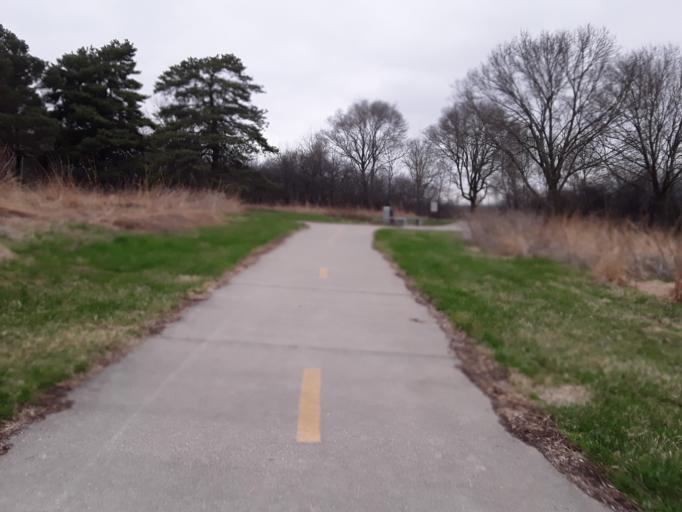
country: US
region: Nebraska
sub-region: Lancaster County
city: Lincoln
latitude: 40.8508
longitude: -96.6081
